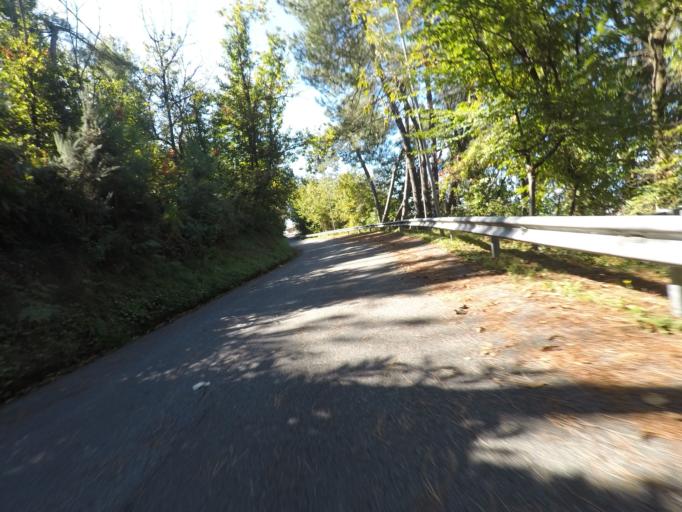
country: IT
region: Tuscany
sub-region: Provincia di Massa-Carrara
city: Montignoso
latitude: 44.0375
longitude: 10.1618
